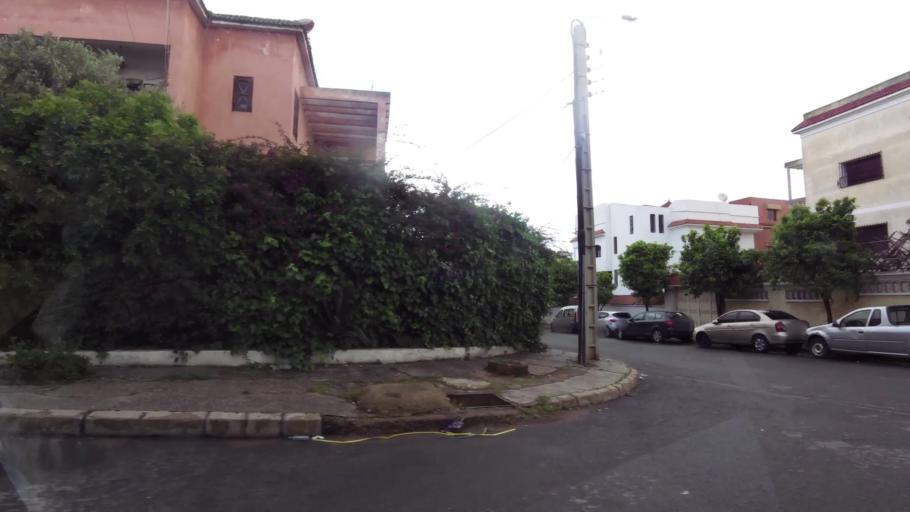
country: MA
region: Grand Casablanca
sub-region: Casablanca
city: Casablanca
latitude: 33.5624
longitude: -7.6795
